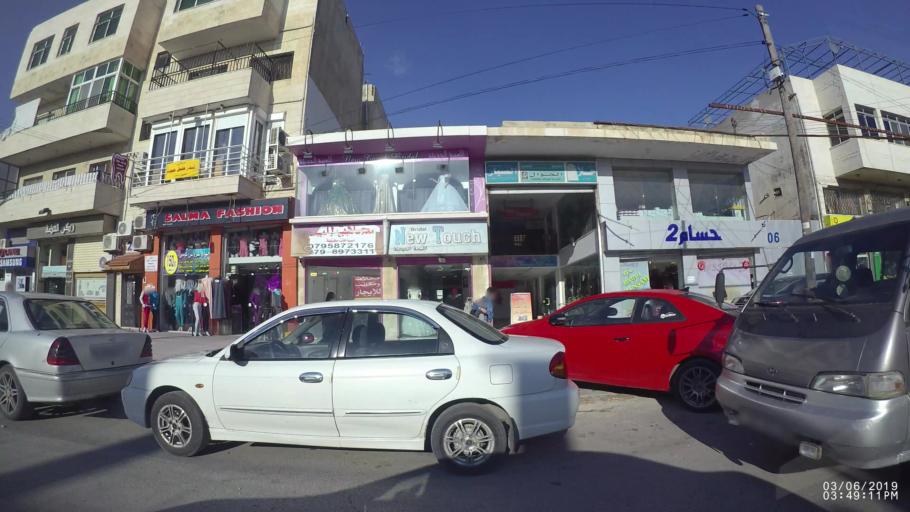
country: JO
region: Amman
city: Amman
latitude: 31.9726
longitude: 35.9508
